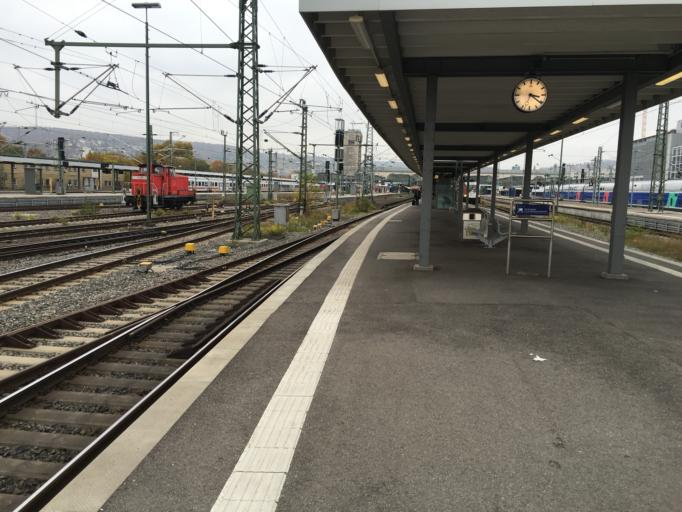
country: DE
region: Baden-Wuerttemberg
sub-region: Regierungsbezirk Stuttgart
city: Stuttgart
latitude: 48.7878
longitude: 9.1853
